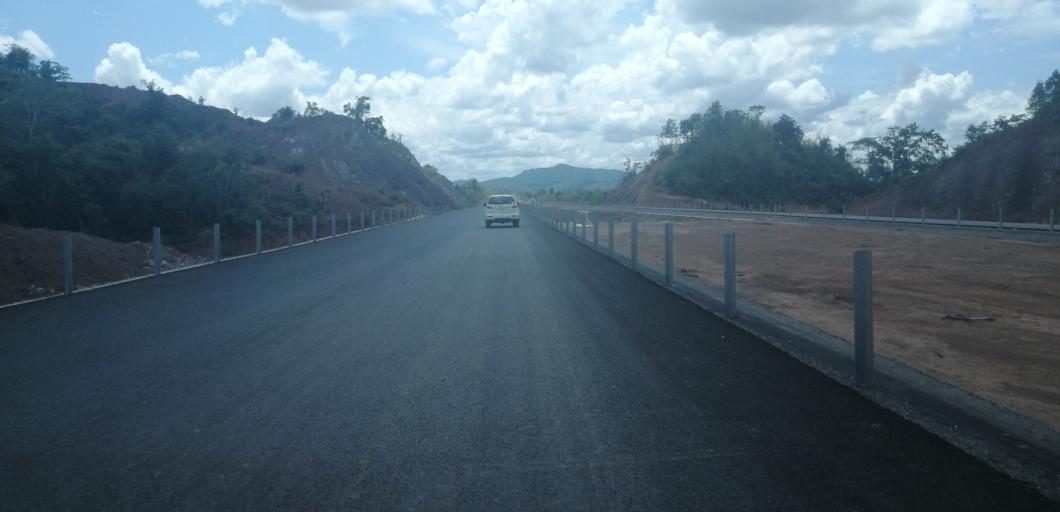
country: LA
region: Vientiane
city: Muang Phon-Hong
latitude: 18.5527
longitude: 102.3499
